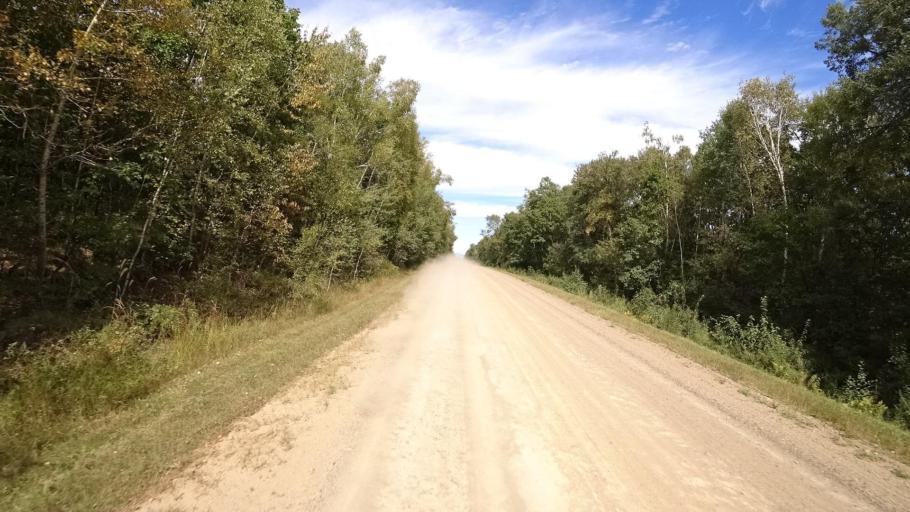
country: RU
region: Primorskiy
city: Yakovlevka
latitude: 44.6700
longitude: 133.6111
